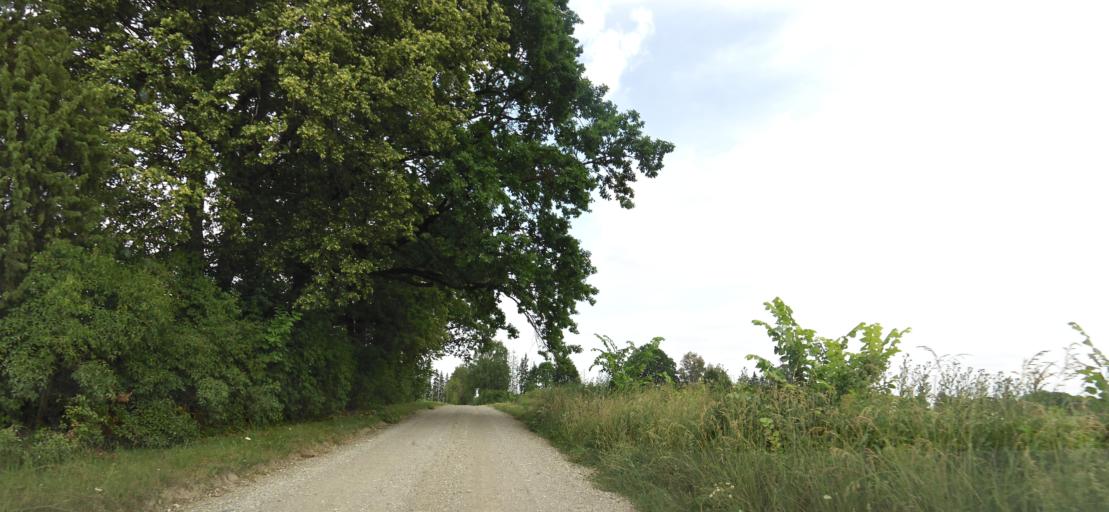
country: LT
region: Panevezys
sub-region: Birzai
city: Birzai
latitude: 56.3572
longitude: 24.7495
